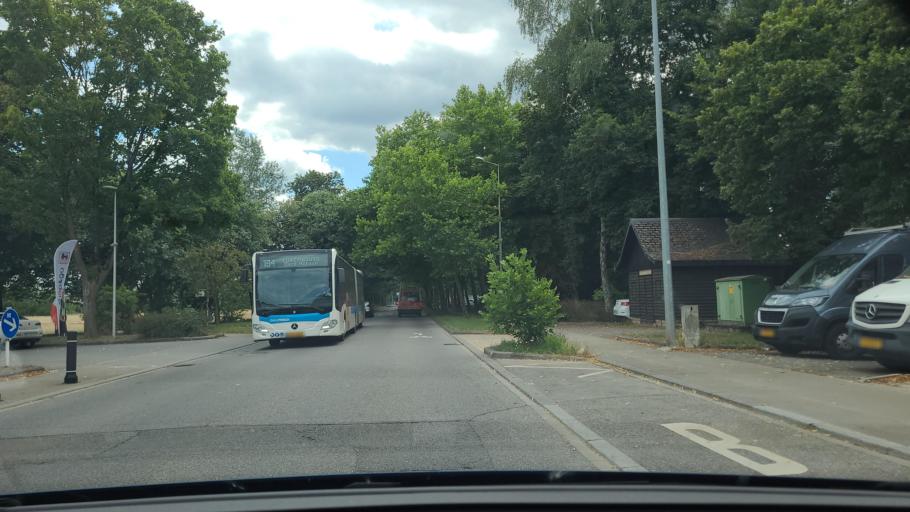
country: LU
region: Luxembourg
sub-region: Canton d'Esch-sur-Alzette
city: Bettembourg
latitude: 49.5256
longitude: 6.1007
